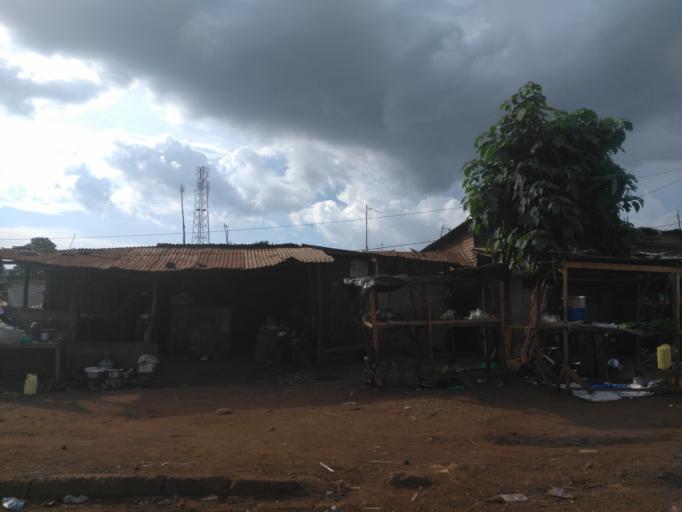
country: UG
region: Eastern Region
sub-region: Jinja District
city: Jinja
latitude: 0.4184
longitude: 33.2135
